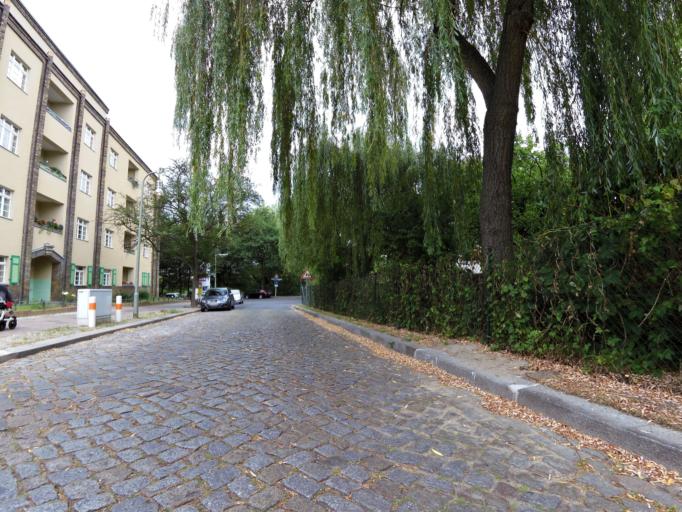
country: DE
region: Berlin
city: Schmargendorf
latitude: 52.4712
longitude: 13.3025
